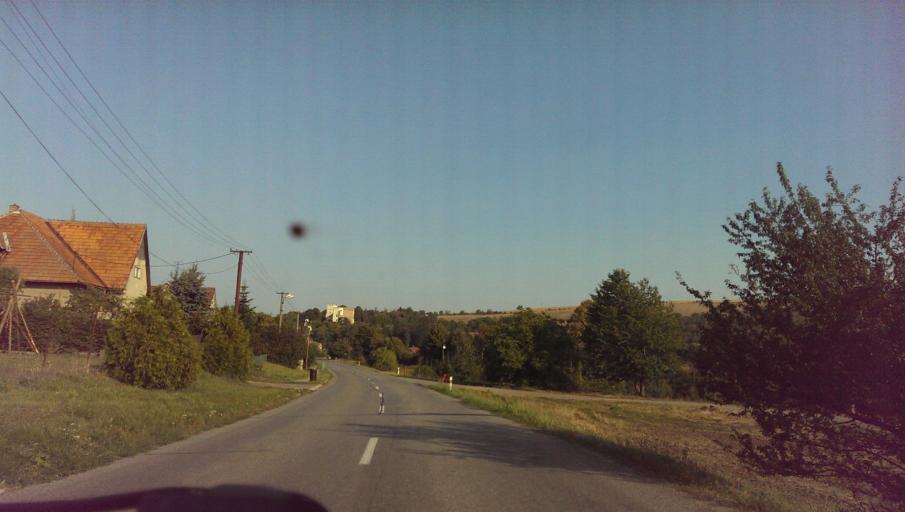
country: CZ
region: South Moravian
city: Nesovice
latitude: 49.1478
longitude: 17.0989
